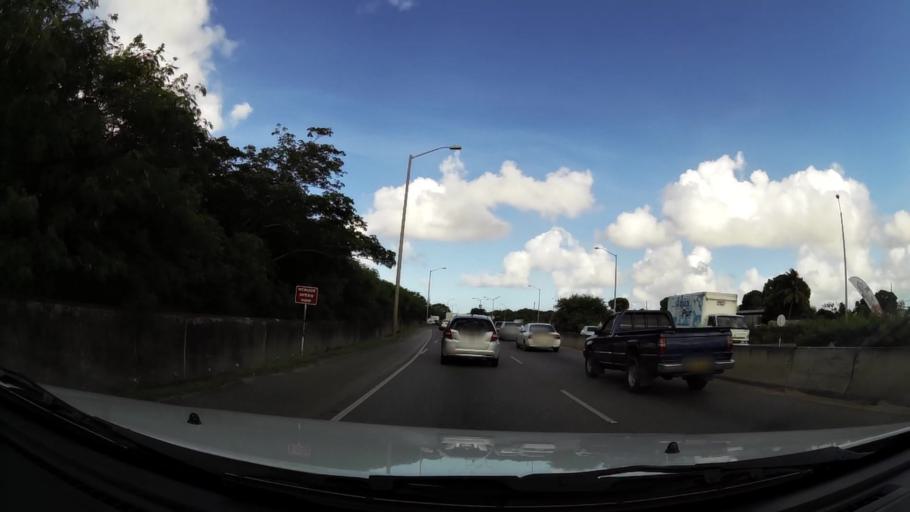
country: BB
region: Saint Michael
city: Bridgetown
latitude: 13.1256
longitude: -59.5944
